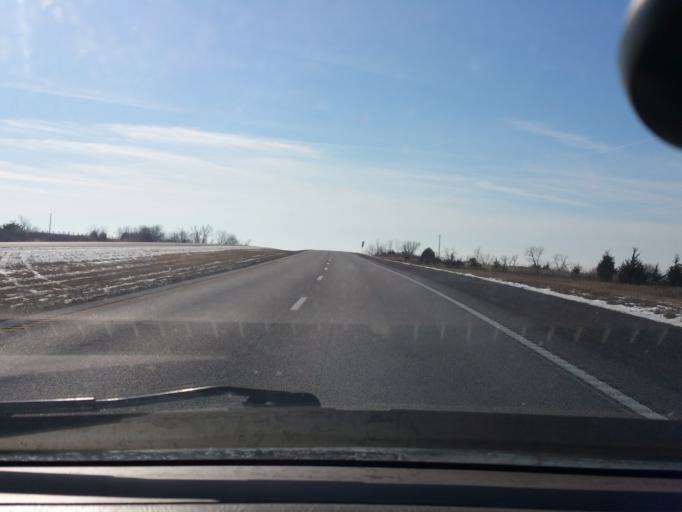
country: US
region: Missouri
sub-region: Daviess County
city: Gallatin
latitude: 39.9233
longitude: -94.1391
